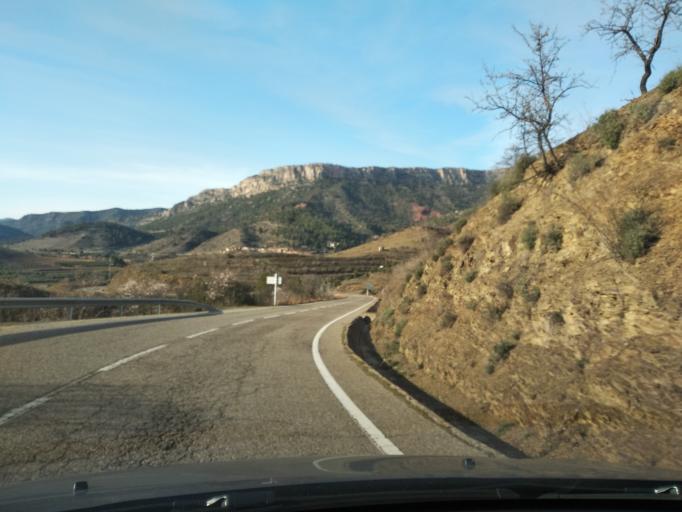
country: ES
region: Catalonia
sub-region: Provincia de Tarragona
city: Margalef
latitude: 41.2143
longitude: 0.7686
